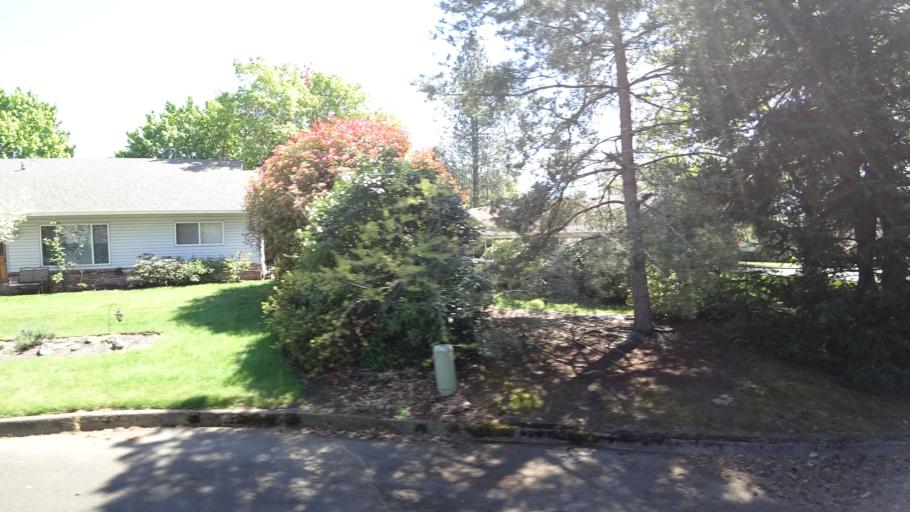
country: US
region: Oregon
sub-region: Washington County
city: Hillsboro
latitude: 45.5005
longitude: -122.9570
